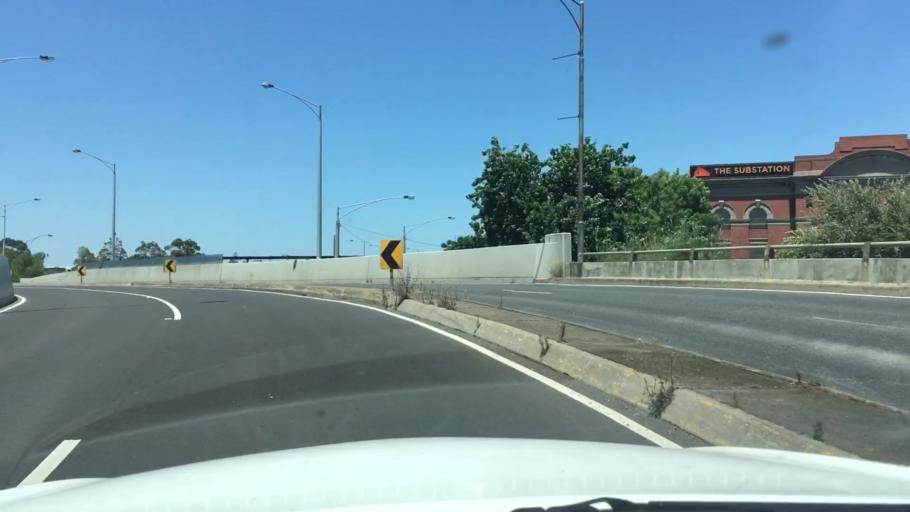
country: AU
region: Victoria
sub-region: Hobsons Bay
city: Newport
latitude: -37.8434
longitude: 144.8833
